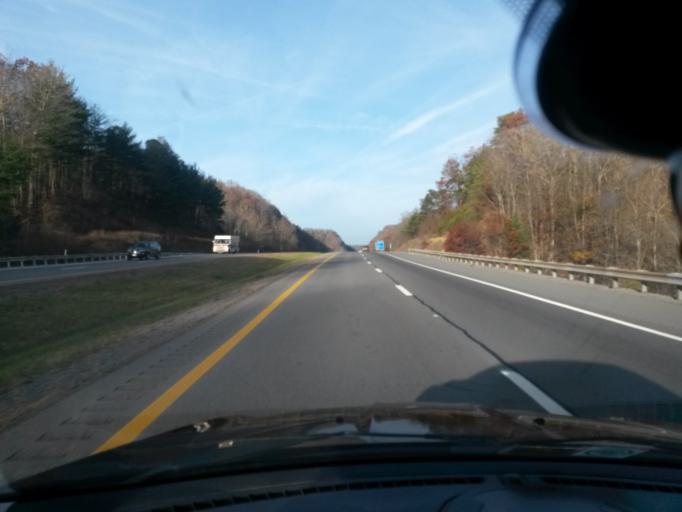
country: US
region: West Virginia
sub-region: Greenbrier County
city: Lewisburg
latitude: 37.8599
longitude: -80.5256
